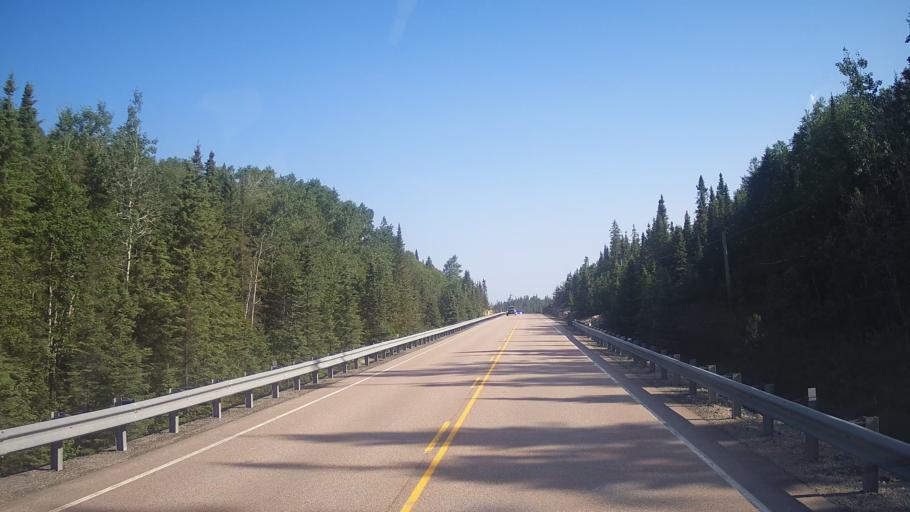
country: CA
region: Ontario
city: Rayside-Balfour
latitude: 47.0056
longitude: -81.6330
